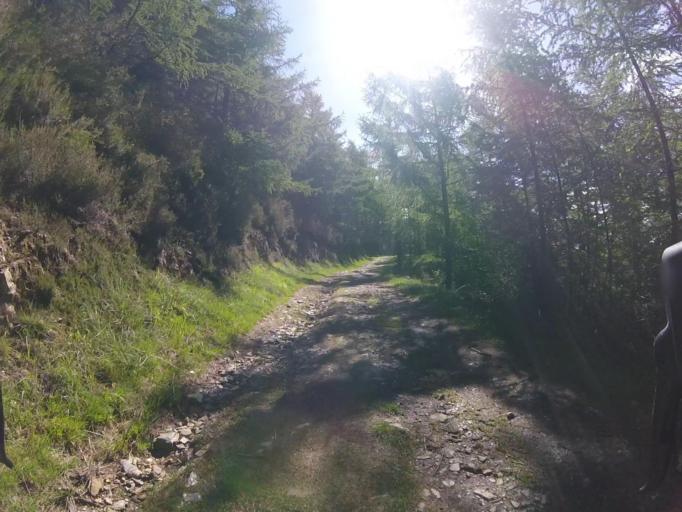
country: ES
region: Navarre
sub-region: Provincia de Navarra
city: Arano
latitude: 43.1799
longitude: -1.9457
